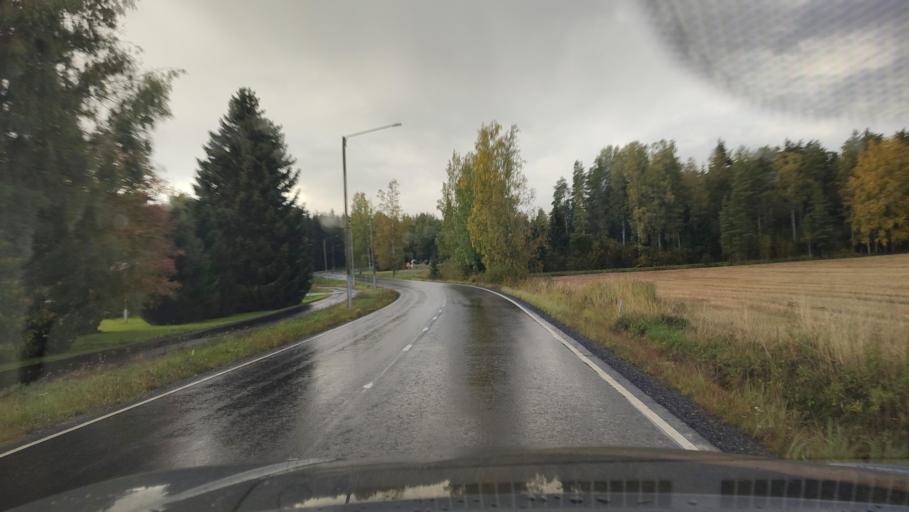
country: FI
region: Southern Ostrobothnia
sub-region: Suupohja
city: Karijoki
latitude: 62.3101
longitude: 21.7091
